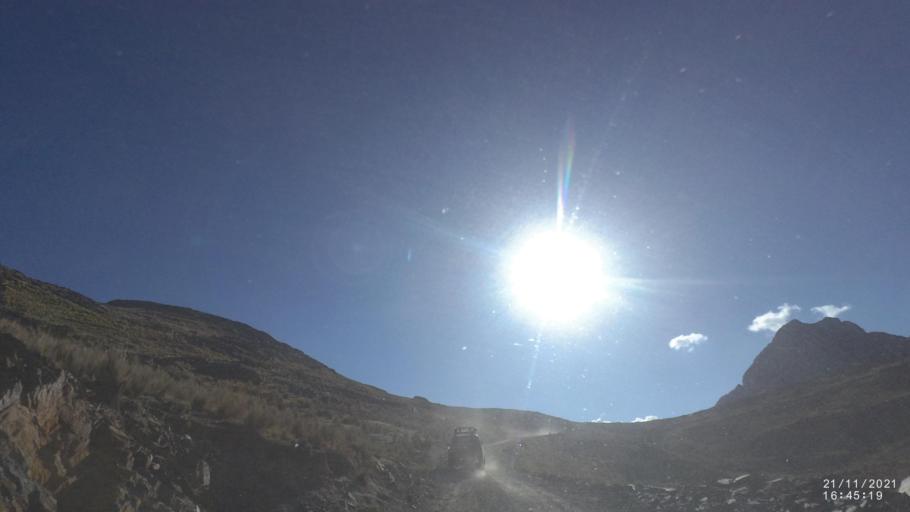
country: BO
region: Cochabamba
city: Cochabamba
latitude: -17.0756
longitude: -66.2558
